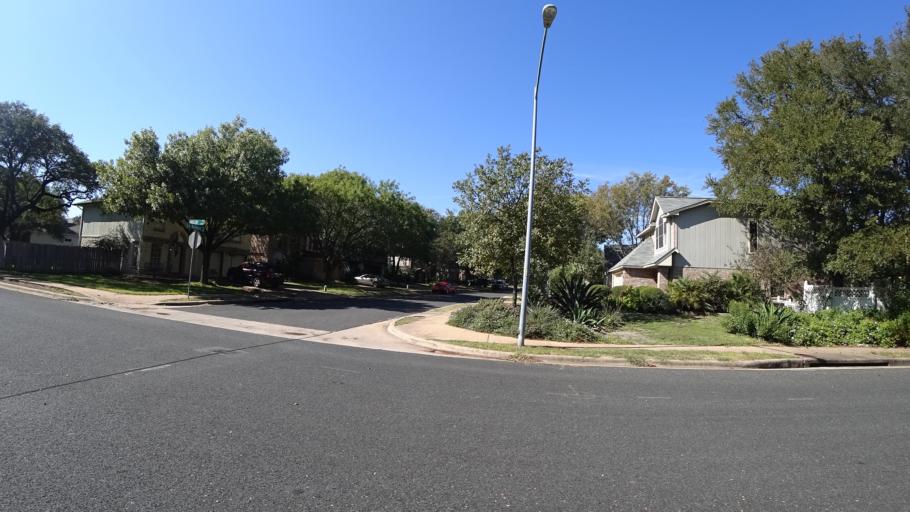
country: US
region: Texas
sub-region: Travis County
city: Shady Hollow
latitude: 30.2140
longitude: -97.8730
